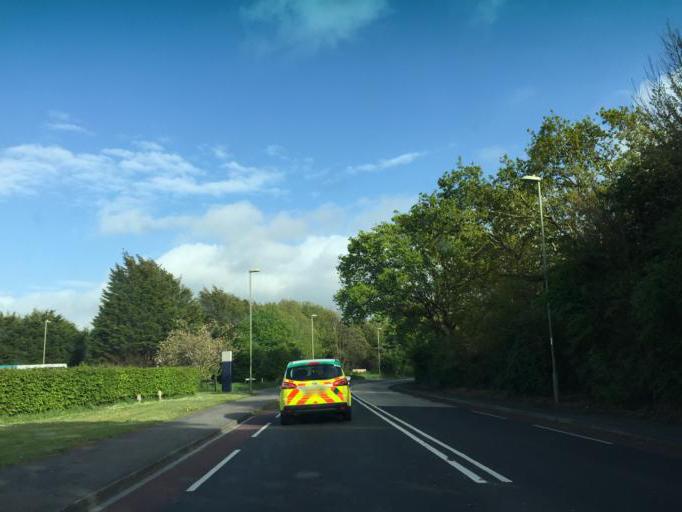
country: GB
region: England
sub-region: Hampshire
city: Fareham
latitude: 50.8302
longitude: -1.1690
